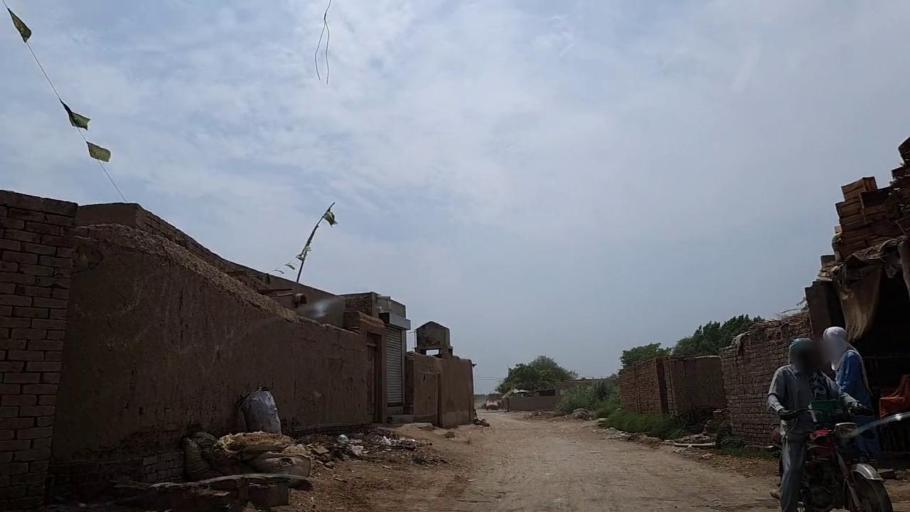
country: PK
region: Sindh
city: Tharu Shah
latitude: 26.9066
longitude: 68.0924
